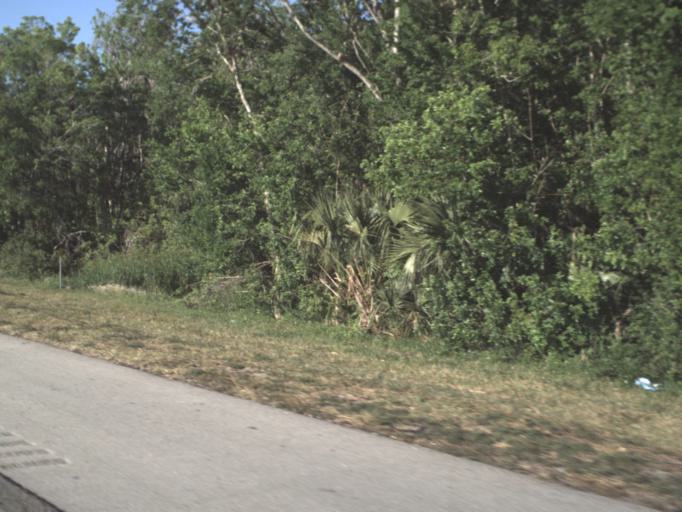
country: US
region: Florida
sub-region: Brevard County
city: South Patrick Shores
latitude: 28.1809
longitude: -80.7057
